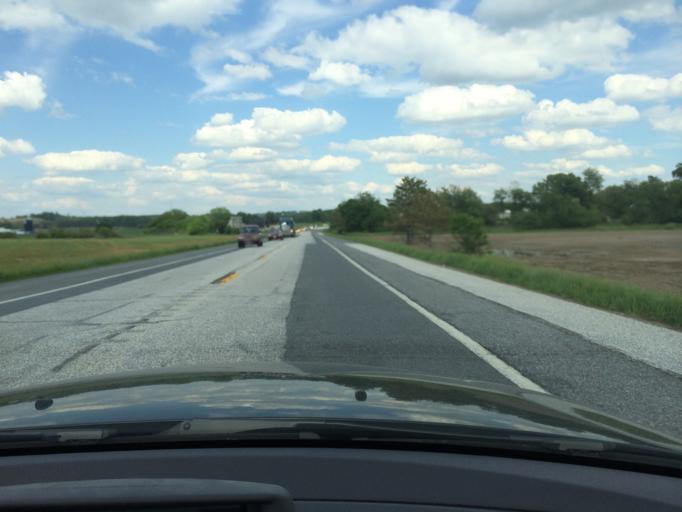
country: US
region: Maryland
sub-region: Carroll County
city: New Windsor
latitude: 39.5470
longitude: -77.0795
